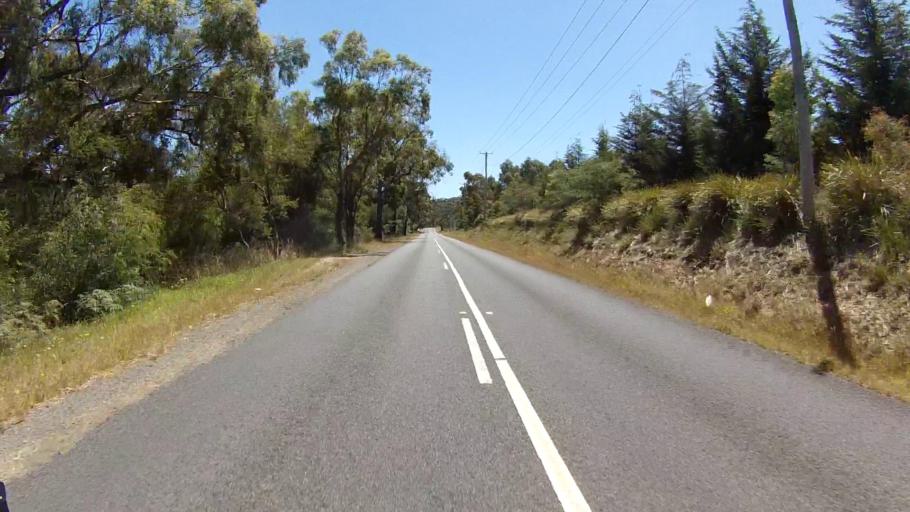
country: AU
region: Tasmania
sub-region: Clarence
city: Howrah
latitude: -42.8687
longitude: 147.4248
